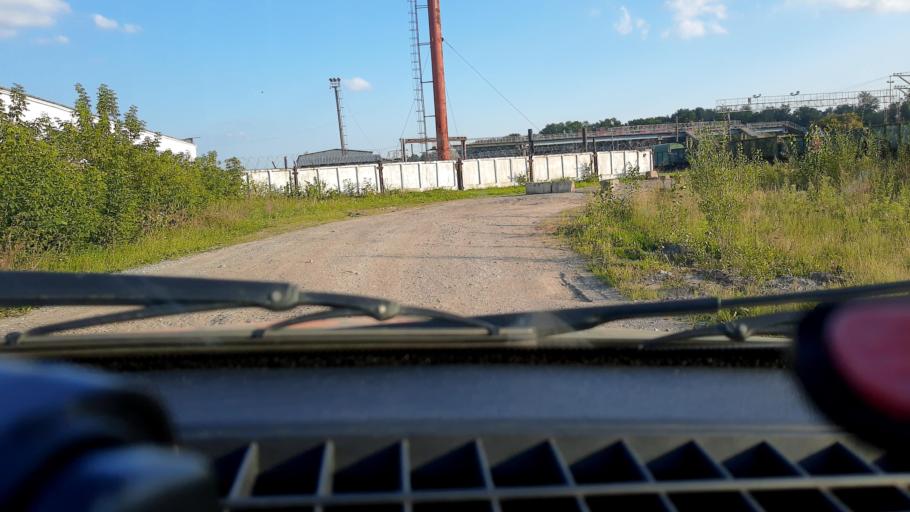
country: RU
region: Bashkortostan
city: Ufa
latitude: 54.5665
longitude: 55.9260
